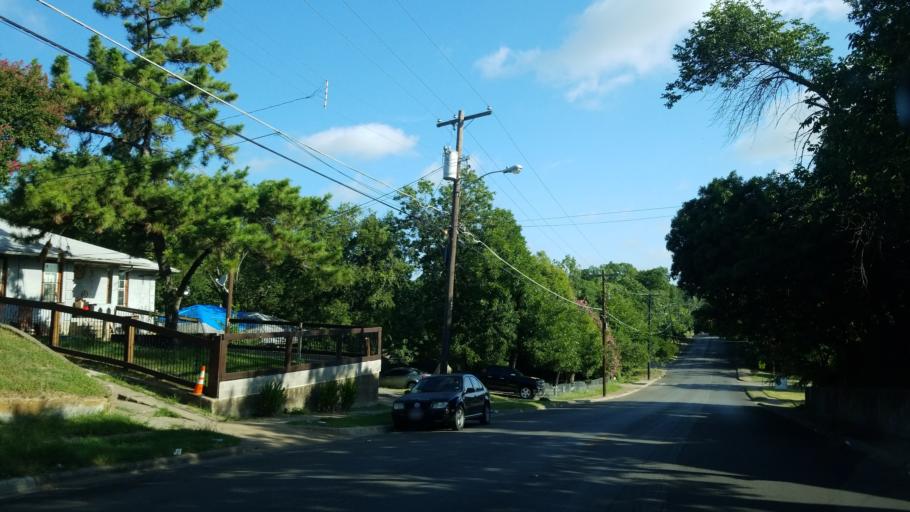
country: US
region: Texas
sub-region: Dallas County
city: Dallas
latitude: 32.7319
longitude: -96.8055
